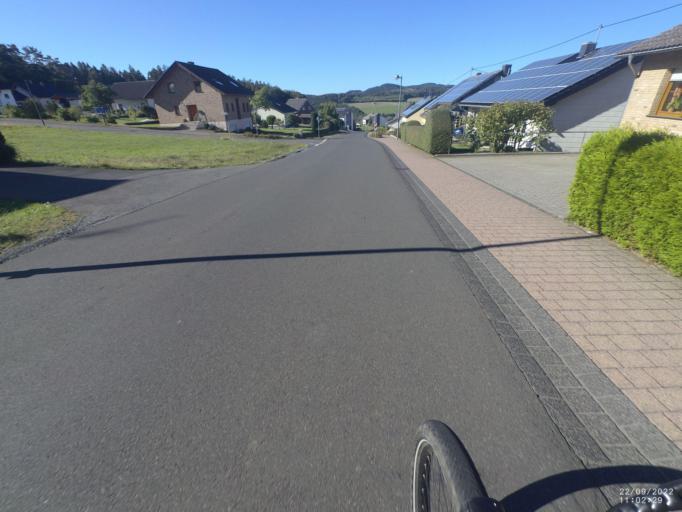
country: DE
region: Rheinland-Pfalz
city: Dockweiler
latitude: 50.2298
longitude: 6.8020
